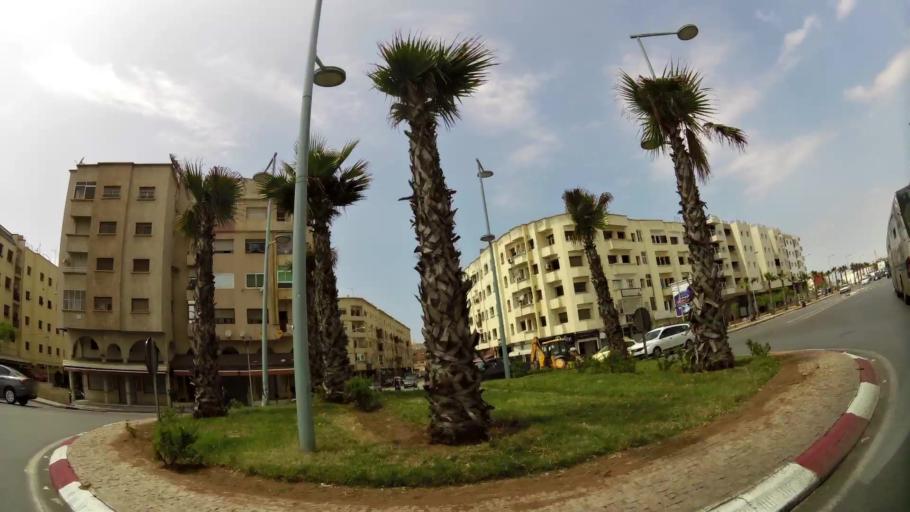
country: MA
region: Rabat-Sale-Zemmour-Zaer
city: Sale
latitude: 34.0516
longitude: -6.8123
